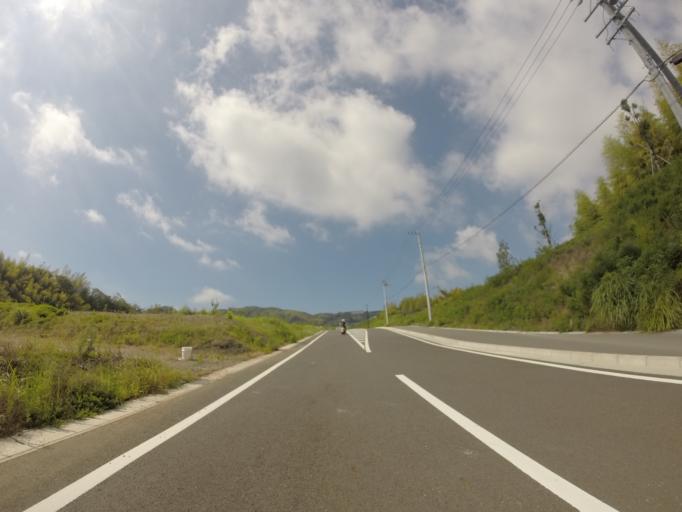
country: JP
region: Shizuoka
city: Shizuoka-shi
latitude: 34.9934
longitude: 138.4715
